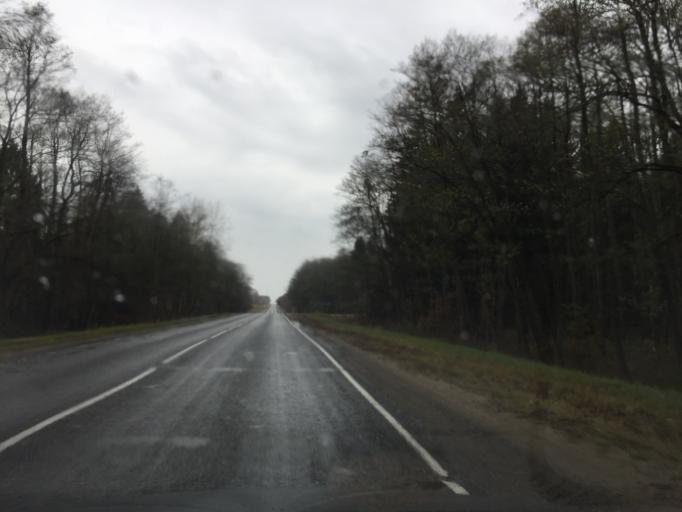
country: BY
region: Mogilev
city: Slawharad
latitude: 53.4078
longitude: 30.9364
